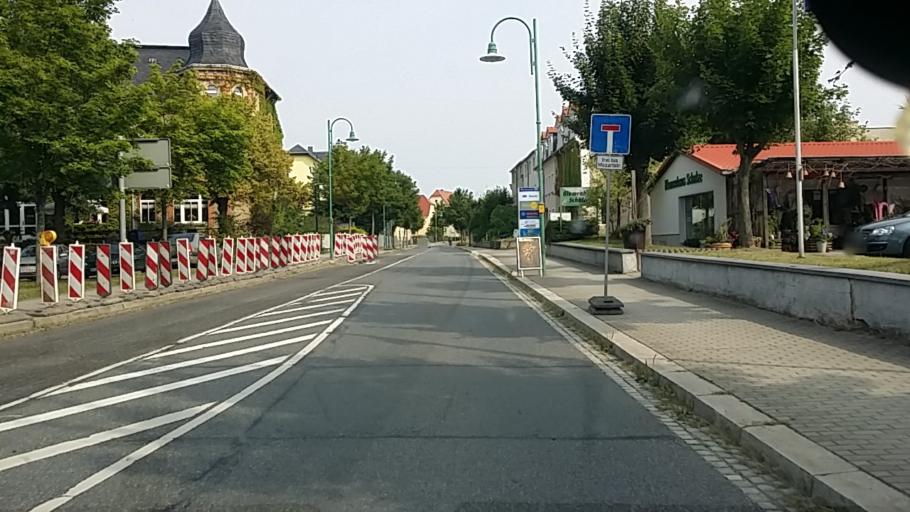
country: DE
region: Saxony
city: Radeberg
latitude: 51.1227
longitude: 13.9175
